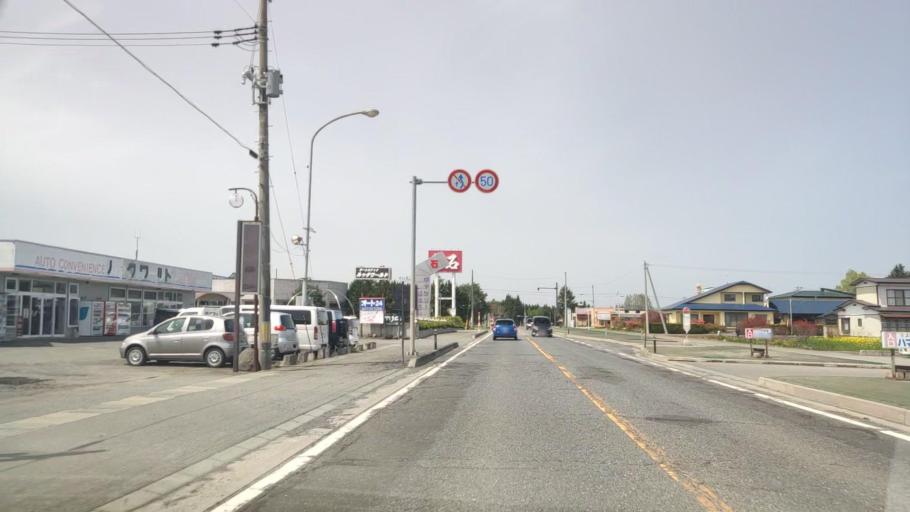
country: JP
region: Aomori
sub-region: Misawa Shi
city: Inuotose
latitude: 40.6756
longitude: 141.1759
